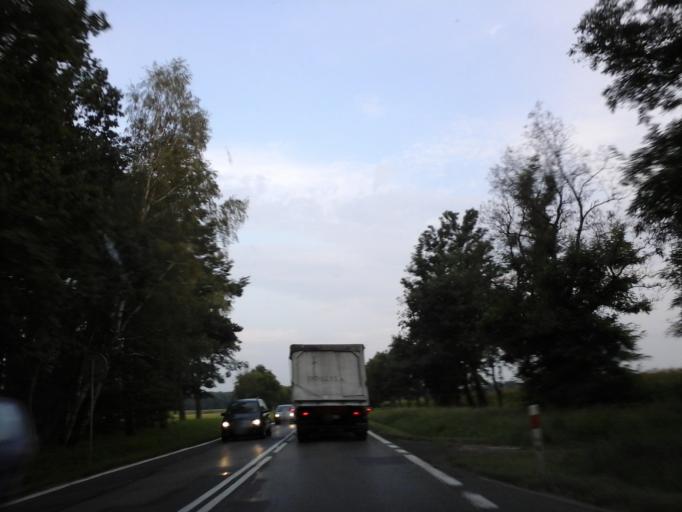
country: PL
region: Lower Silesian Voivodeship
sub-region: Powiat trzebnicki
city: Prusice
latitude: 51.4157
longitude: 16.9320
